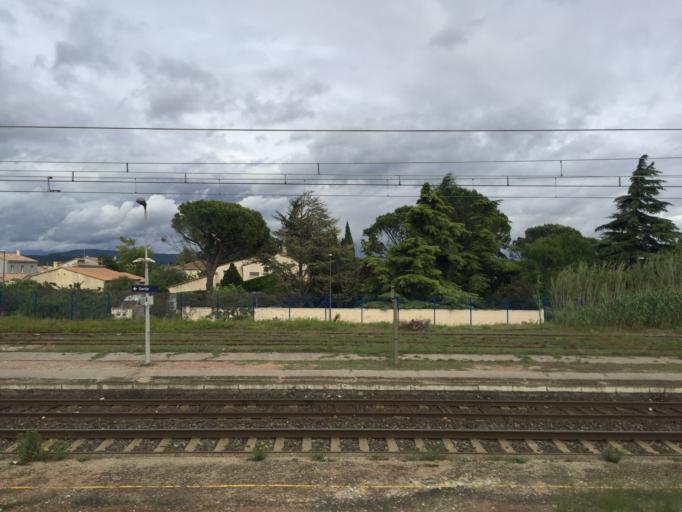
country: FR
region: Rhone-Alpes
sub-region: Departement de la Drome
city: Pierrelatte
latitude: 44.3731
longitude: 4.7037
